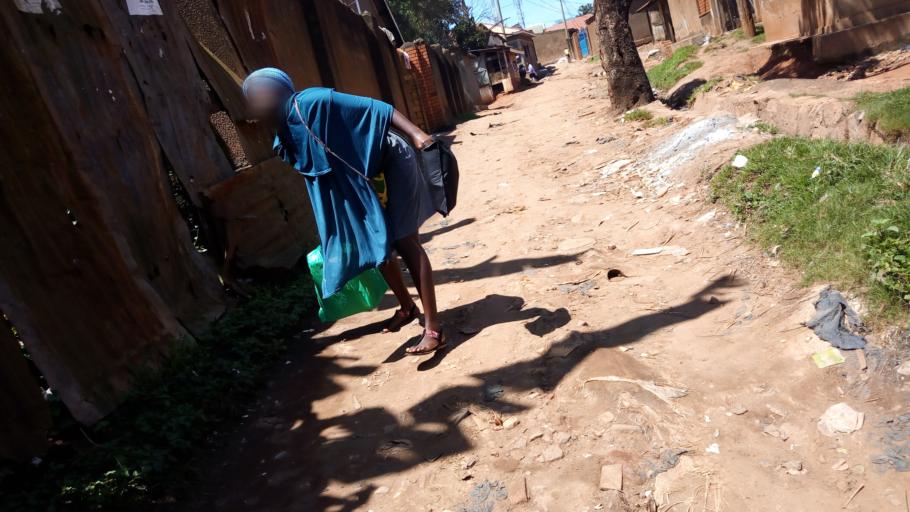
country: UG
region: Central Region
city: Kampala Central Division
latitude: 0.3555
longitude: 32.5587
